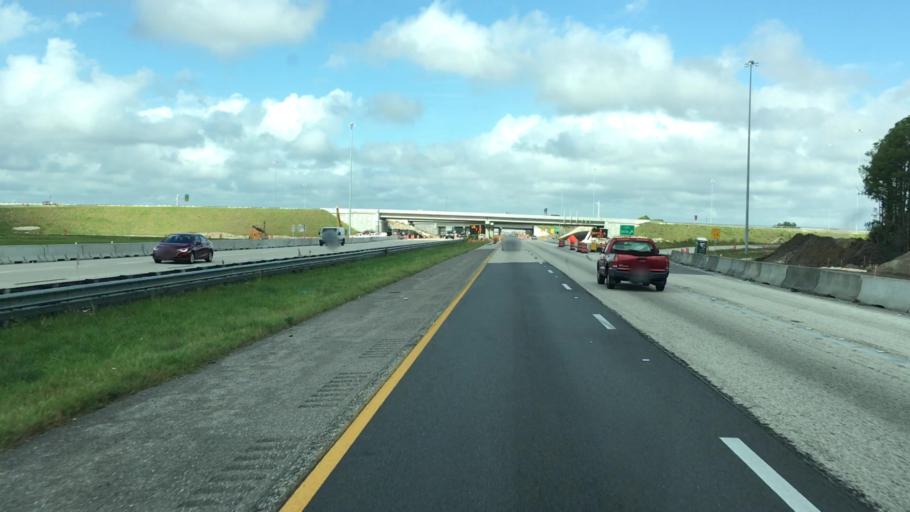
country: US
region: Florida
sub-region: Volusia County
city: South Daytona
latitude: 29.1527
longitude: -81.0741
